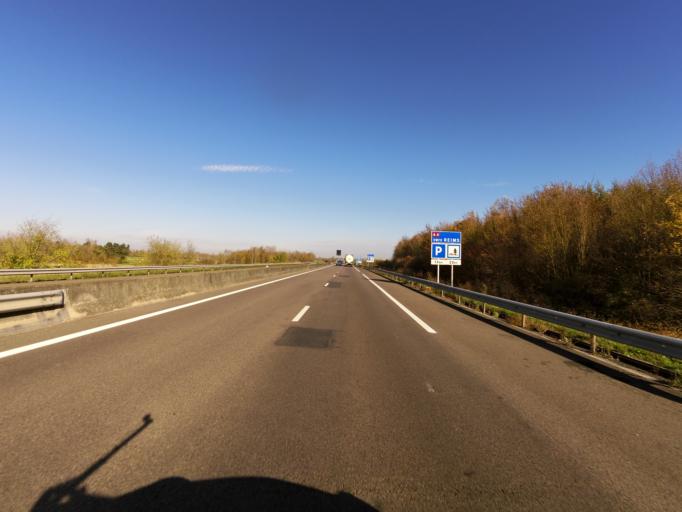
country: FR
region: Champagne-Ardenne
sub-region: Departement de la Marne
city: Fagnieres
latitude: 48.9988
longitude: 4.2975
